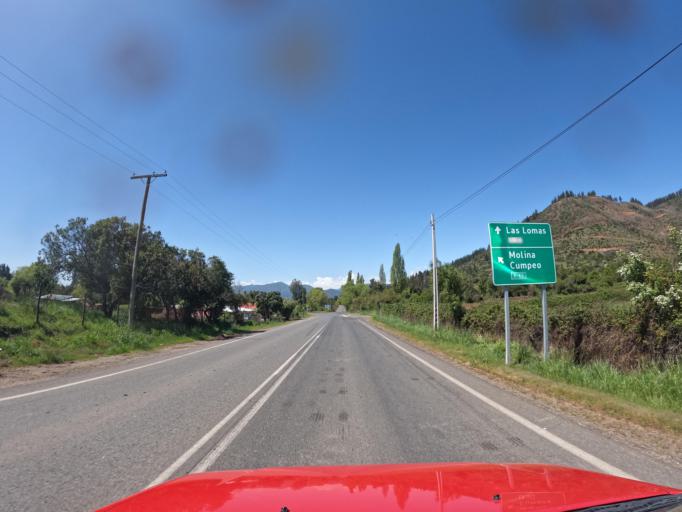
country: CL
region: Maule
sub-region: Provincia de Talca
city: San Clemente
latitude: -35.4843
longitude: -71.2730
